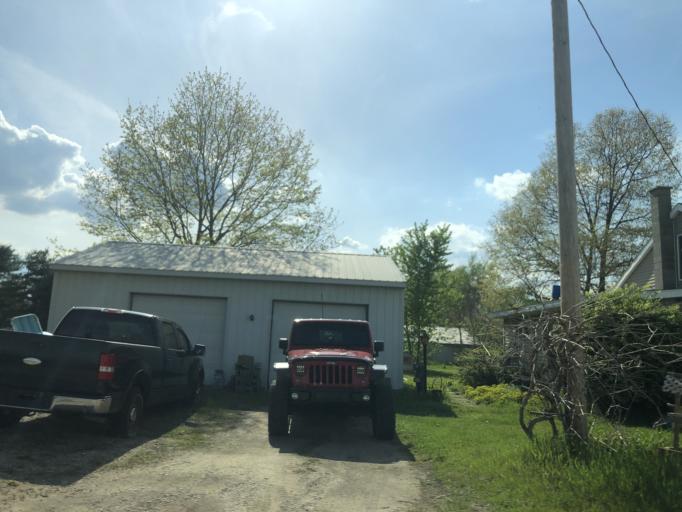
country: US
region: Michigan
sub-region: Hillsdale County
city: Reading
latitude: 41.7534
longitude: -84.8097
